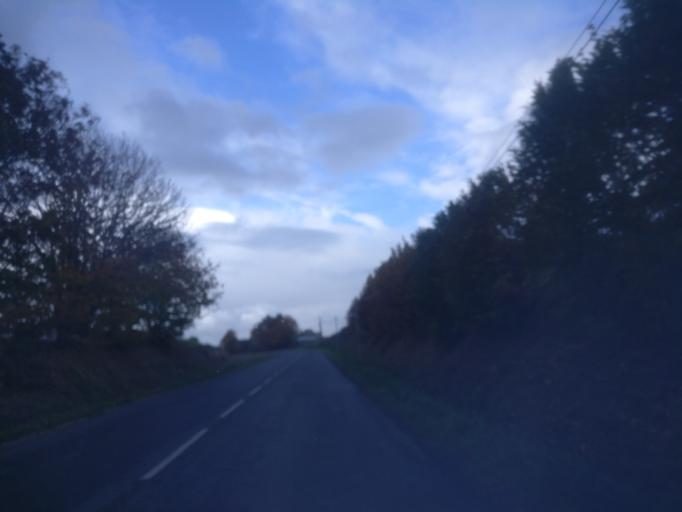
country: FR
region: Brittany
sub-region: Departement d'Ille-et-Vilaine
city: Goven
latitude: 48.0358
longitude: -1.8326
